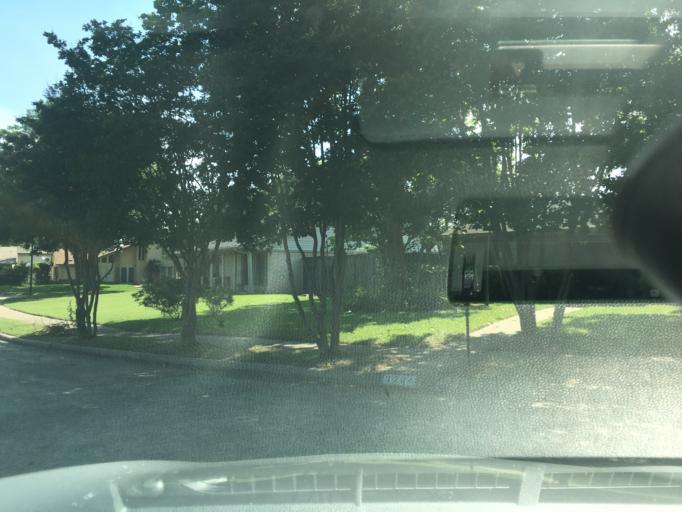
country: US
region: Texas
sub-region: Dallas County
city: Richardson
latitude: 32.9620
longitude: -96.6774
